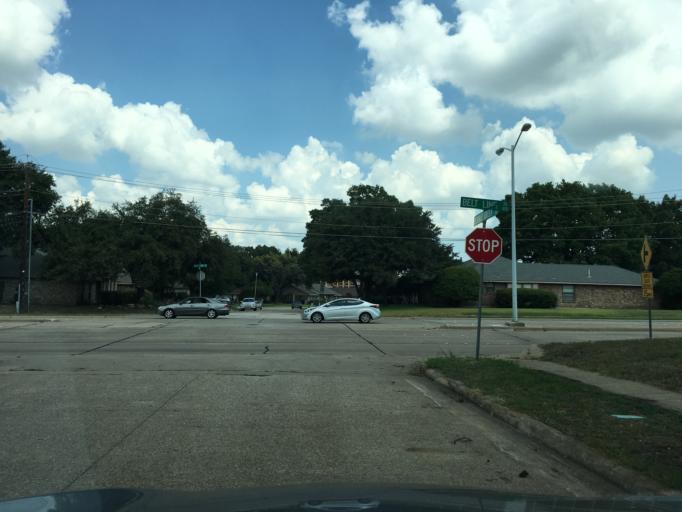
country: US
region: Texas
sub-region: Dallas County
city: Garland
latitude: 32.9398
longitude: -96.6378
